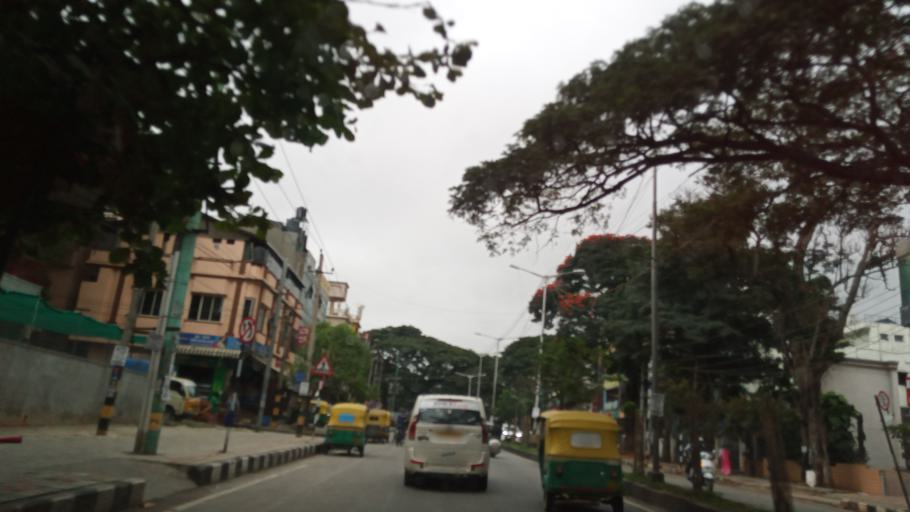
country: IN
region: Karnataka
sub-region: Bangalore Urban
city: Bangalore
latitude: 12.9233
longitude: 77.5555
